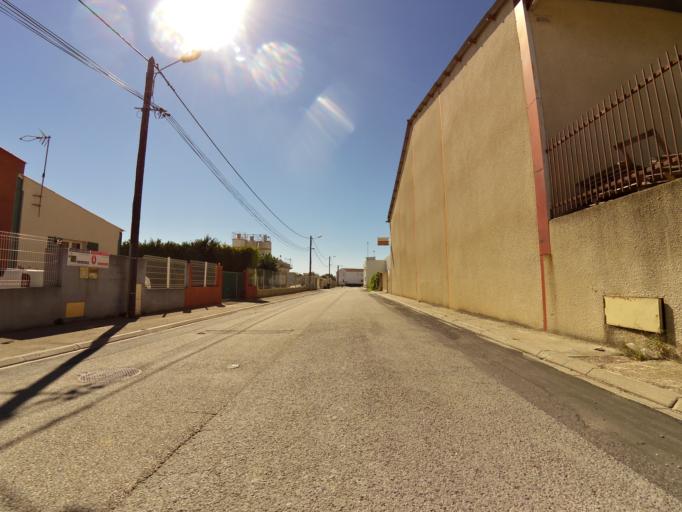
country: FR
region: Languedoc-Roussillon
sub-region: Departement du Gard
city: Codognan
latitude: 43.7264
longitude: 4.2147
